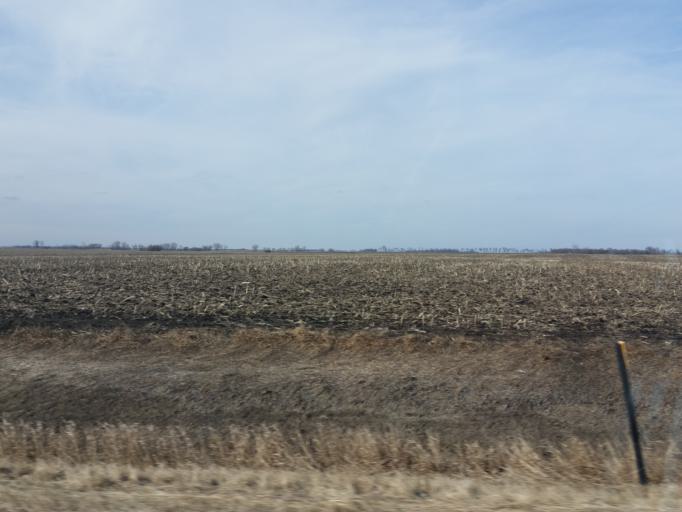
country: US
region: Minnesota
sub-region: Clay County
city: Barnesville
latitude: 46.4715
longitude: -96.3317
